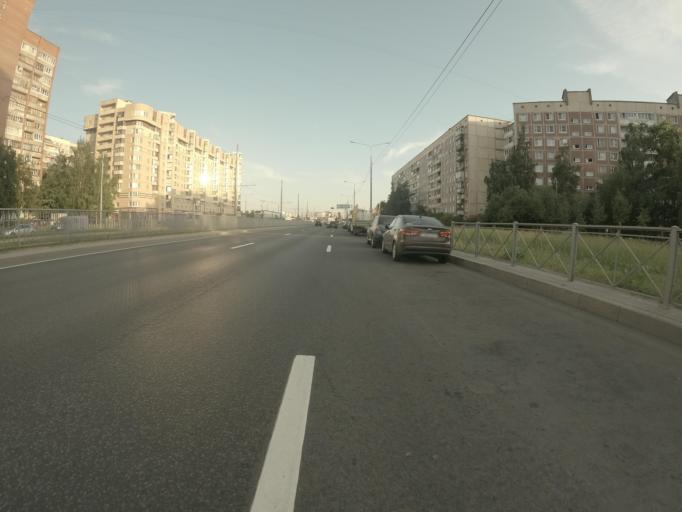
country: RU
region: St.-Petersburg
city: Krasnogvargeisky
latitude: 59.9382
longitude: 30.4885
